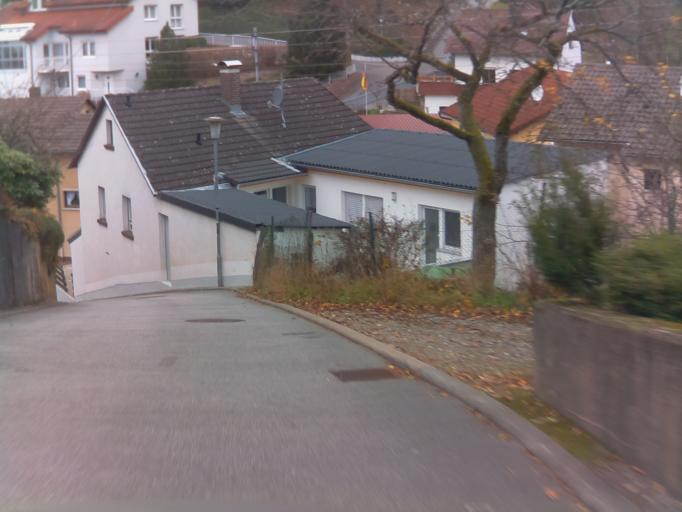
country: DE
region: Baden-Wuerttemberg
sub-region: Karlsruhe Region
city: Wilhelmsfeld
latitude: 49.4875
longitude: 8.7386
